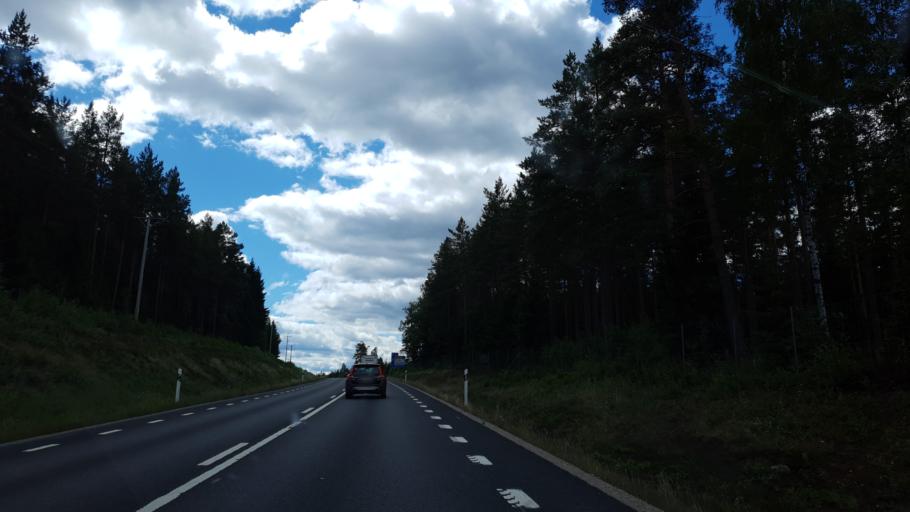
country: SE
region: Kronoberg
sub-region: Vaxjo Kommun
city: Braas
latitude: 57.1841
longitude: 15.1569
